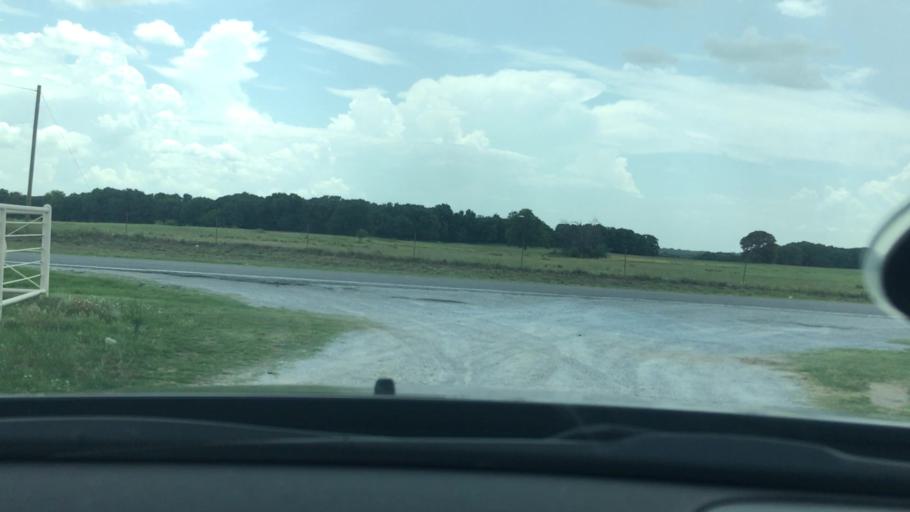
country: US
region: Oklahoma
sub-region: Carter County
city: Wilson
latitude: 33.9406
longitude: -97.4165
